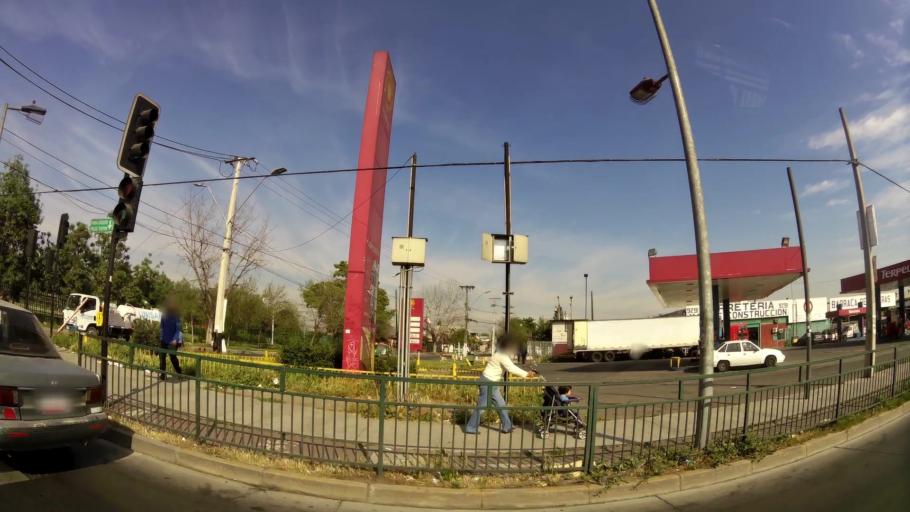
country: CL
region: Santiago Metropolitan
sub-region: Provincia de Santiago
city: La Pintana
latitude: -33.5475
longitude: -70.6335
